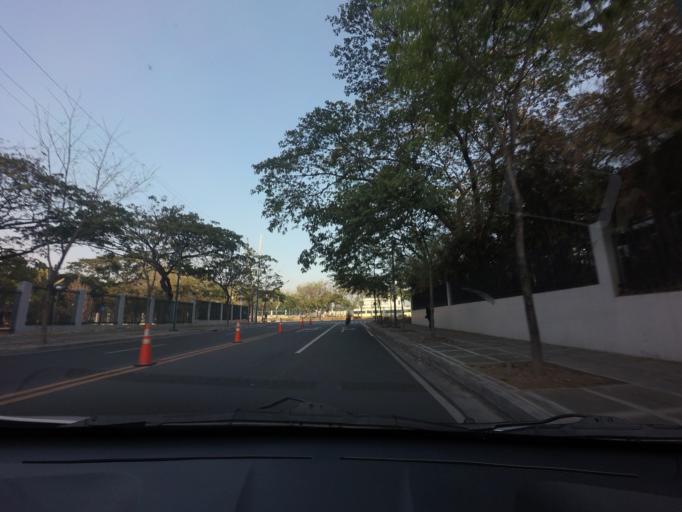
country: PH
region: Calabarzon
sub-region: Province of Rizal
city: Pateros
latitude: 14.5560
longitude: 121.0576
